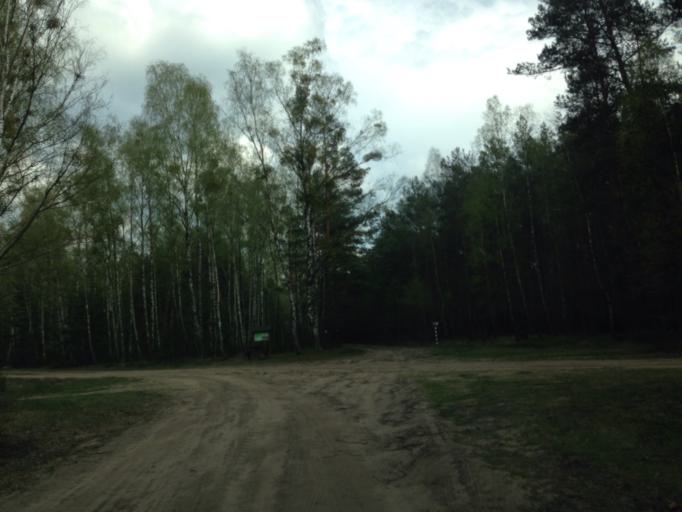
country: PL
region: Kujawsko-Pomorskie
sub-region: Powiat brodnicki
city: Gorzno
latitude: 53.1216
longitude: 19.7101
